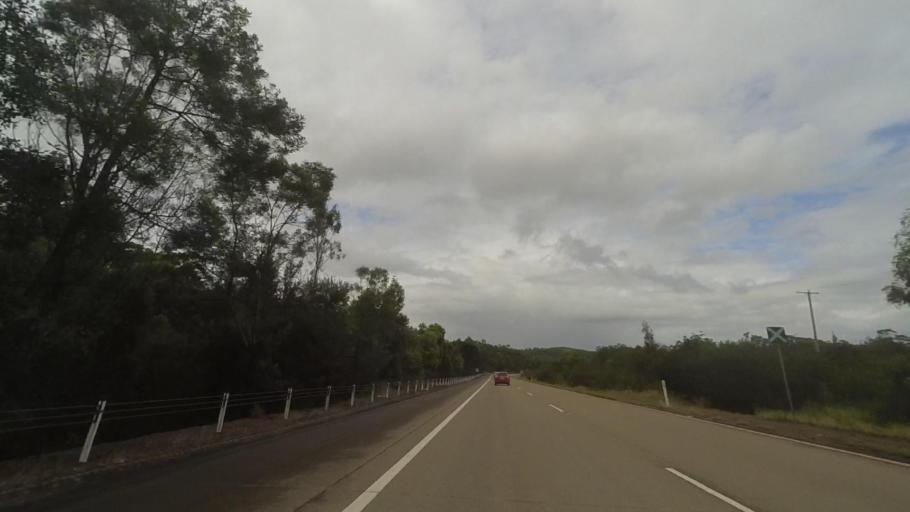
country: AU
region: New South Wales
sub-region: Port Stephens Shire
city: Medowie
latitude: -32.6277
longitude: 151.9429
